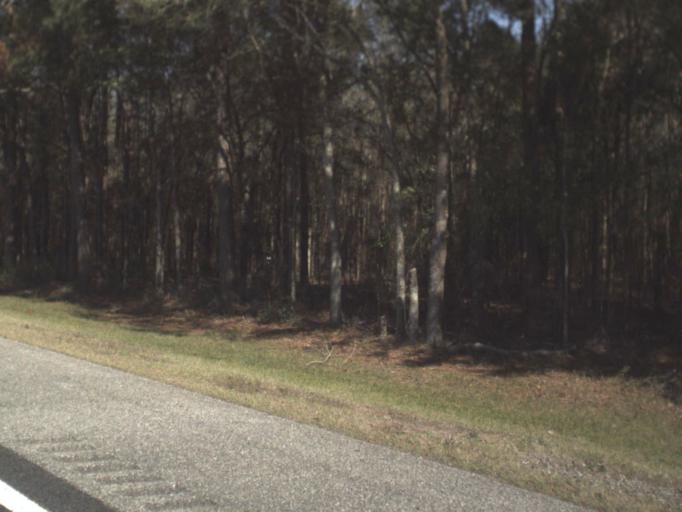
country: US
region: Florida
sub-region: Gadsden County
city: Gretna
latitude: 30.5623
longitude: -84.6461
